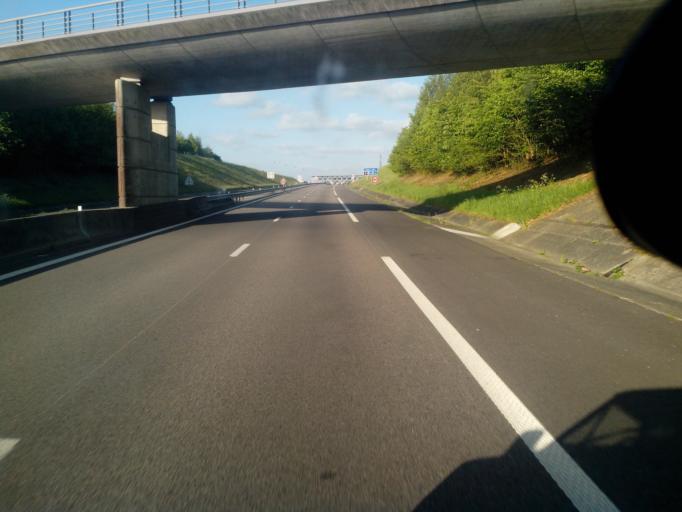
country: FR
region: Haute-Normandie
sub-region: Departement de la Seine-Maritime
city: Saint-Saens
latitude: 49.6449
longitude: 1.2342
